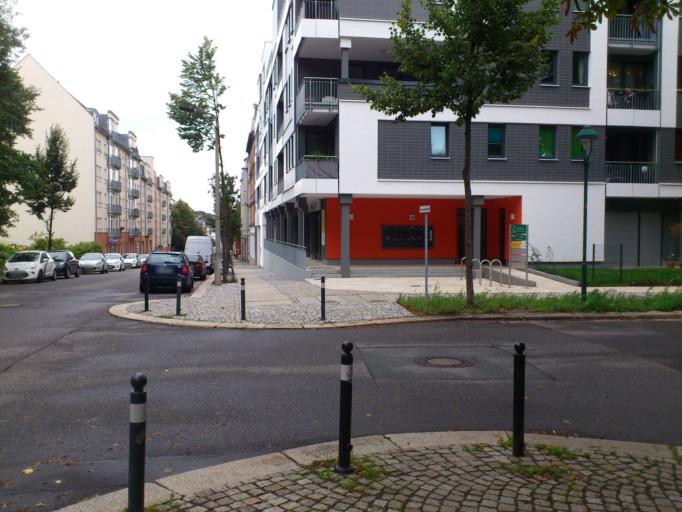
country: DE
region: Saxony
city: Chemnitz
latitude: 50.8343
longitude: 12.9051
